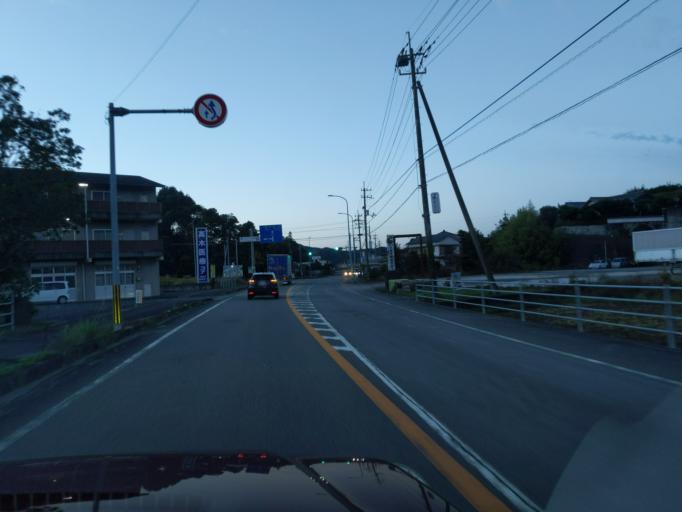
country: JP
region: Tokushima
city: Anan
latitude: 33.8472
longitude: 134.6260
